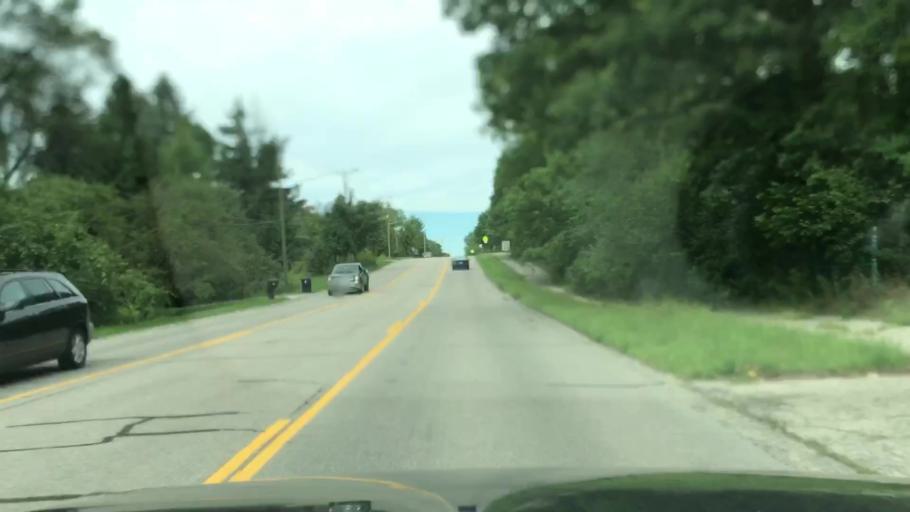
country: US
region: Michigan
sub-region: Kent County
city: East Grand Rapids
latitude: 42.9897
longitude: -85.6005
